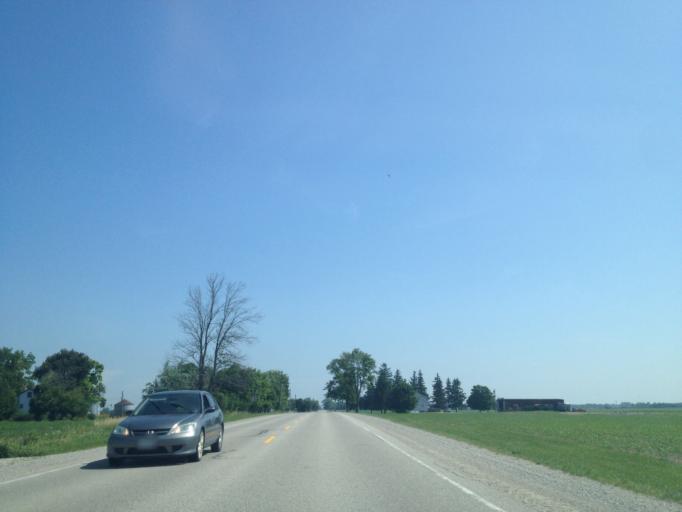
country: CA
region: Ontario
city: London
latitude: 43.2274
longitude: -81.2311
